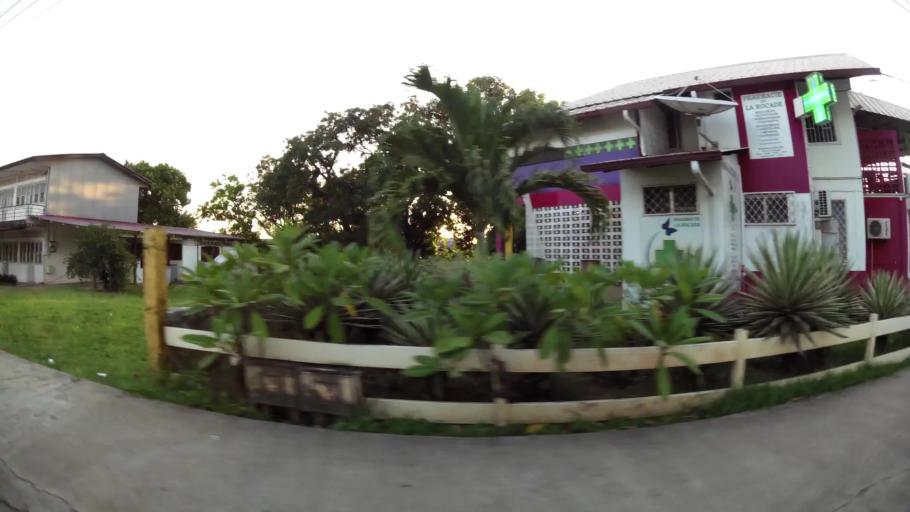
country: GF
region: Guyane
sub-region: Guyane
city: Cayenne
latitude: 4.9303
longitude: -52.3134
